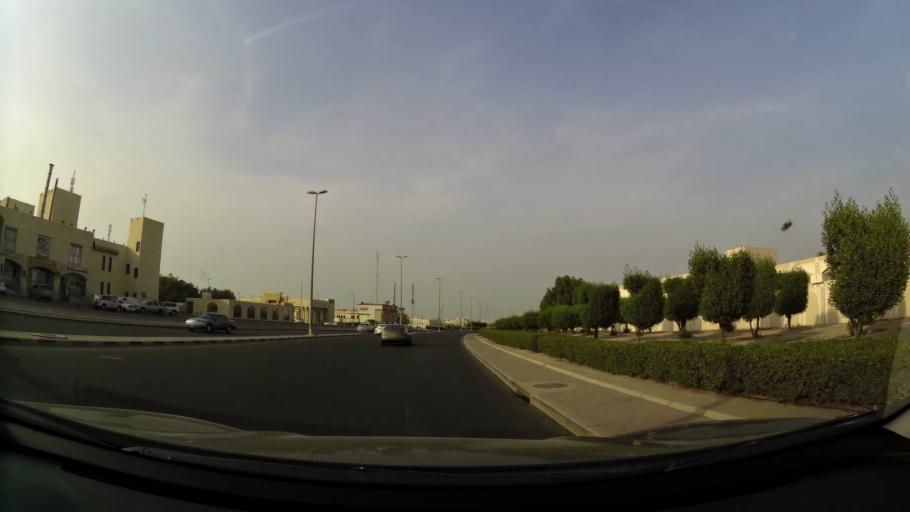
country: KW
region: Mubarak al Kabir
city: Mubarak al Kabir
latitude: 29.2029
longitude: 48.0782
